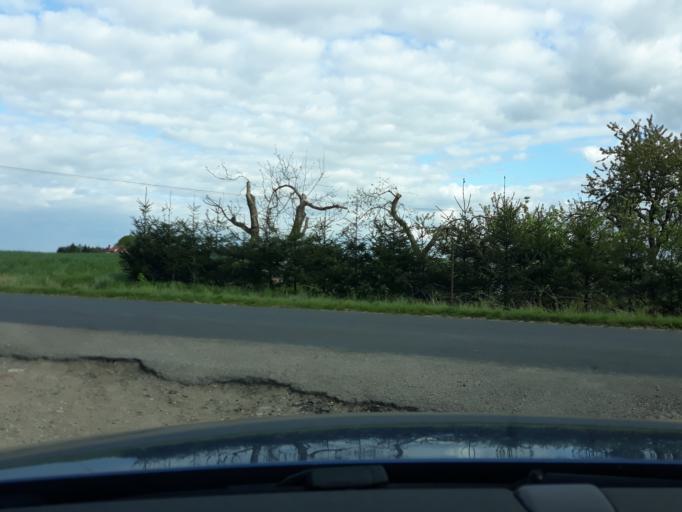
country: PL
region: Pomeranian Voivodeship
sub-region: Powiat czluchowski
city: Czluchow
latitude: 53.7519
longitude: 17.3781
